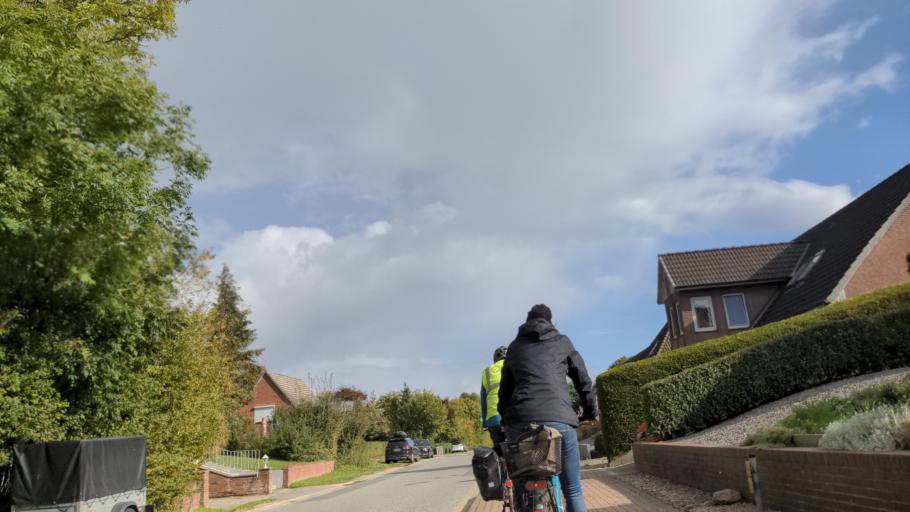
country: DE
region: Schleswig-Holstein
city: Gross Schenkenberg
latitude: 53.7948
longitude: 10.5680
